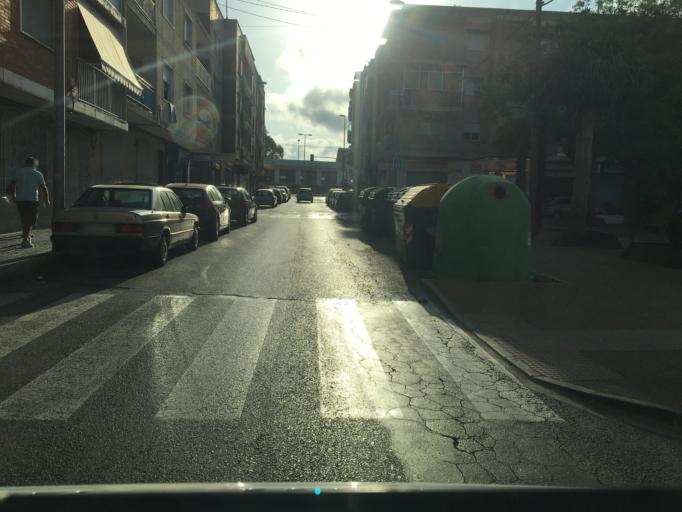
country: ES
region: Murcia
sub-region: Murcia
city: Cartagena
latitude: 37.6211
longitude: -0.9999
